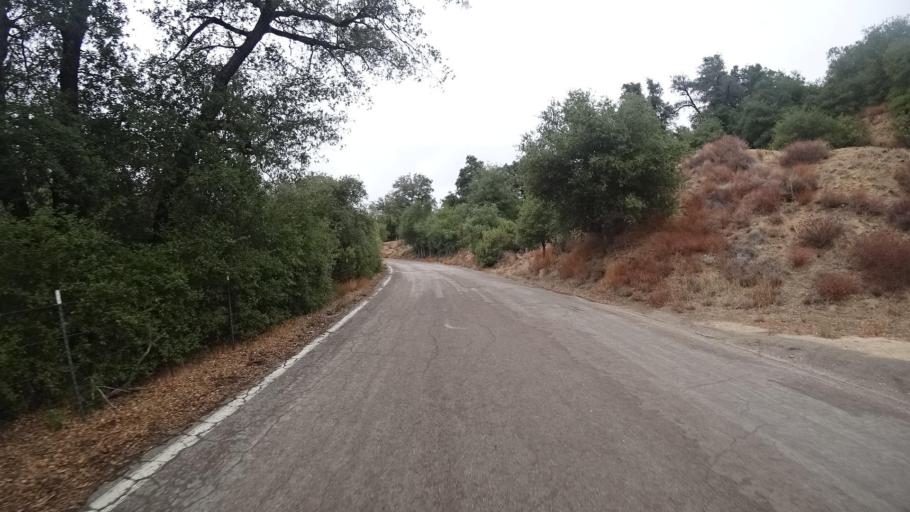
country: US
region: California
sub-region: San Diego County
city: Julian
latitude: 33.0269
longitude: -116.6385
